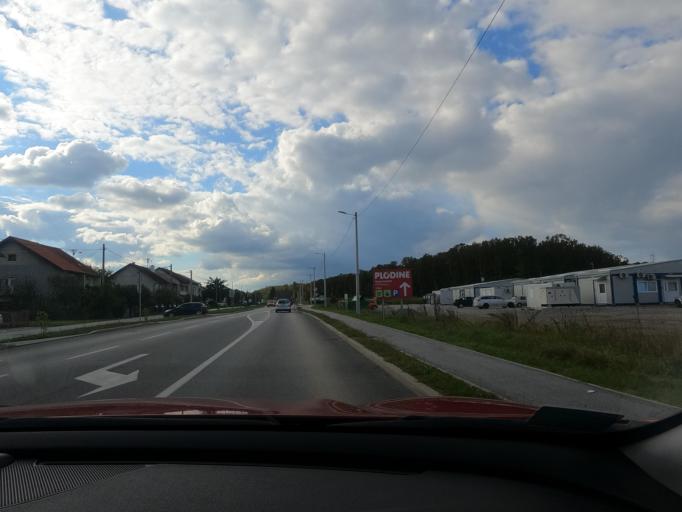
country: HR
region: Sisacko-Moslavacka
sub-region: Grad Sisak
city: Sisak
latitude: 45.4397
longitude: 16.3455
